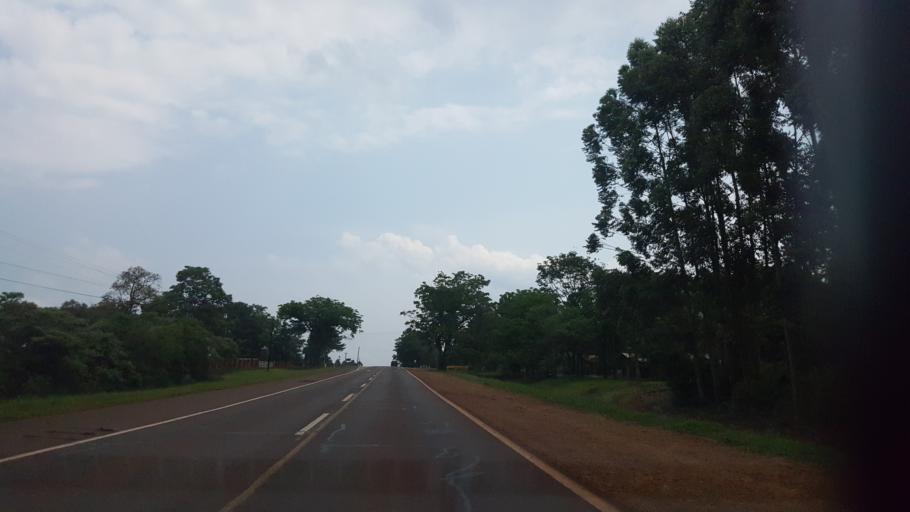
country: AR
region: Misiones
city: Jardin America
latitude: -27.0668
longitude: -55.2671
